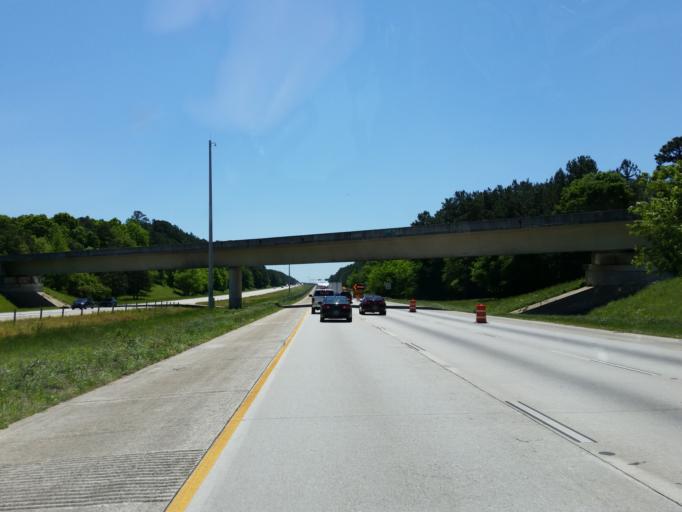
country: US
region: Georgia
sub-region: Clayton County
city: Conley
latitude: 33.6441
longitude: -84.3152
